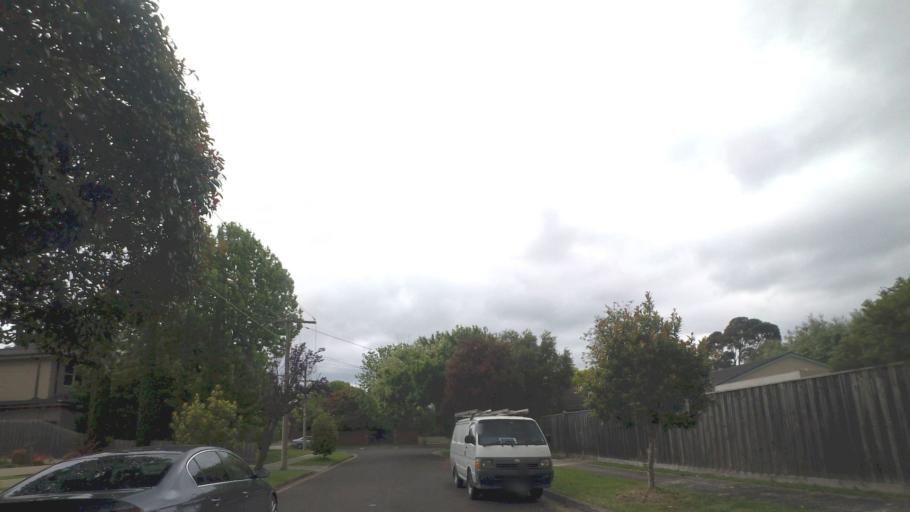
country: AU
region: Victoria
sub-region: Knox
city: Bayswater
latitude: -37.8536
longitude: 145.2496
